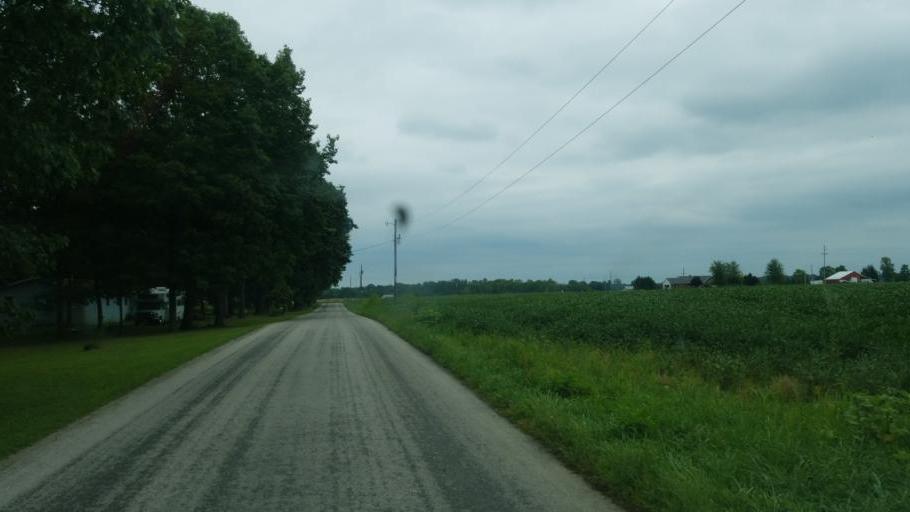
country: US
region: Ohio
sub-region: Morrow County
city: Mount Gilead
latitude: 40.5339
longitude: -82.8018
